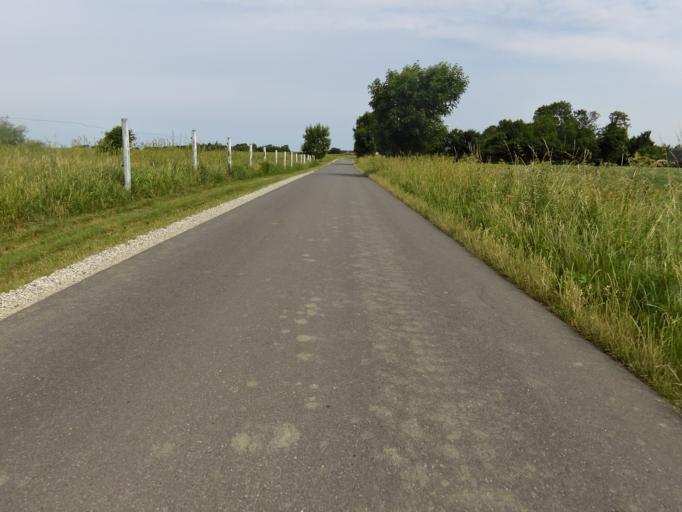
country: DK
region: Central Jutland
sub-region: Holstebro Kommune
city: Holstebro
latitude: 56.4322
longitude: 8.6691
